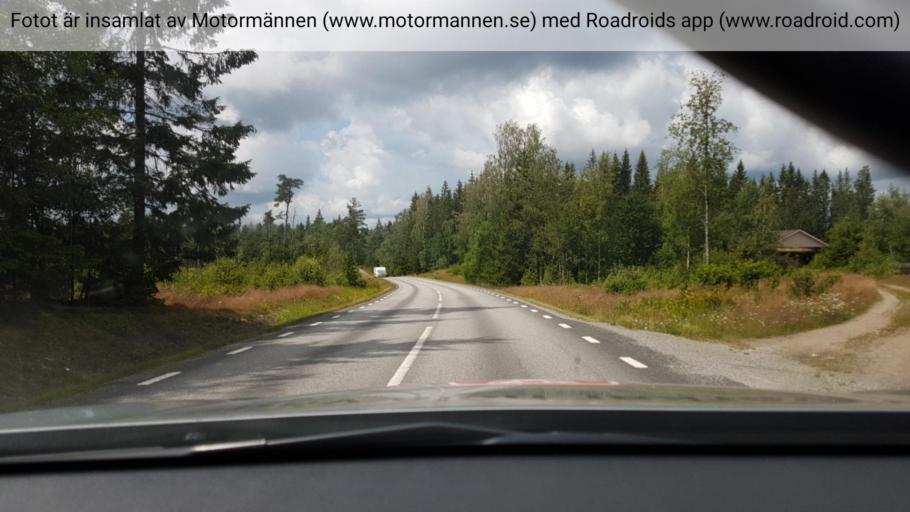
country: SE
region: Vaestra Goetaland
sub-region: Svenljunga Kommun
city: Svenljunga
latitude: 57.4802
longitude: 13.1561
